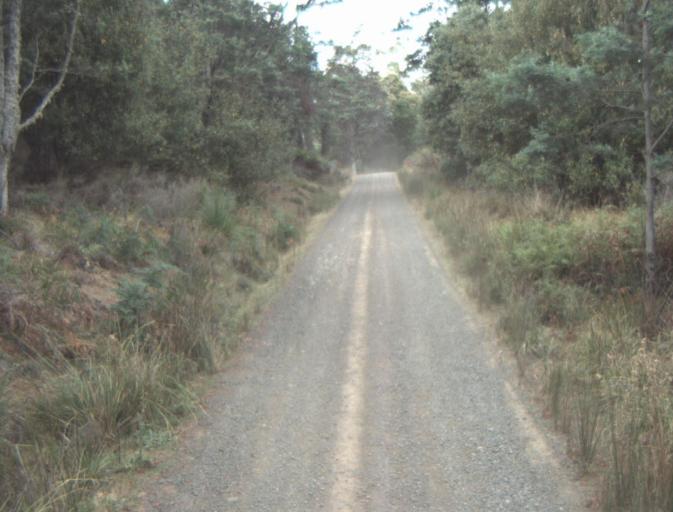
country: AU
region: Tasmania
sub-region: Launceston
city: Mayfield
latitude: -41.2803
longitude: 147.2333
